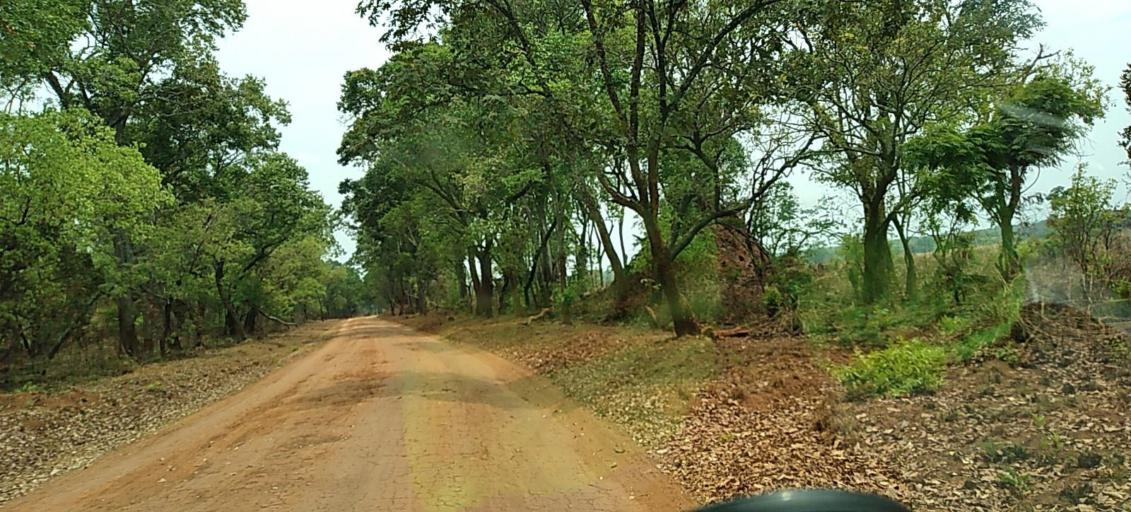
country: ZM
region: North-Western
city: Solwezi
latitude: -12.8123
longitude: 26.5368
